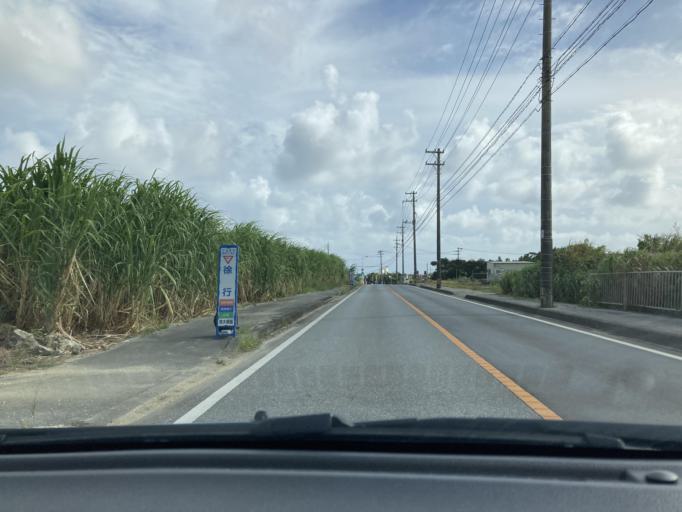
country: JP
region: Okinawa
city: Itoman
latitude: 26.1072
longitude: 127.6946
